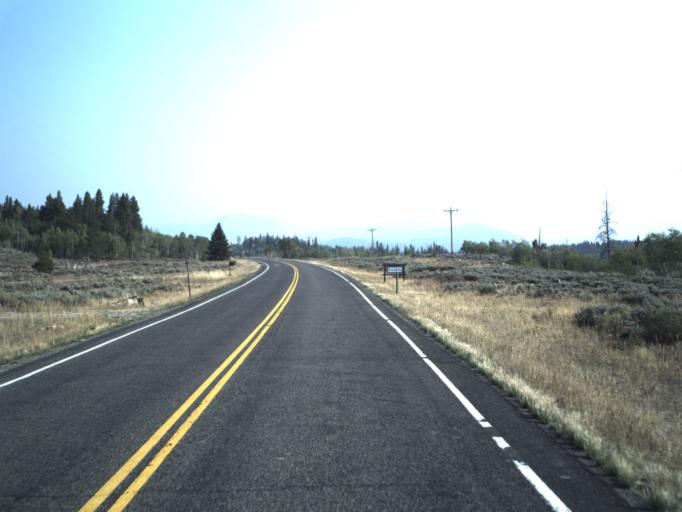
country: US
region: Wyoming
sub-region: Uinta County
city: Evanston
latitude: 40.9361
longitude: -110.8354
